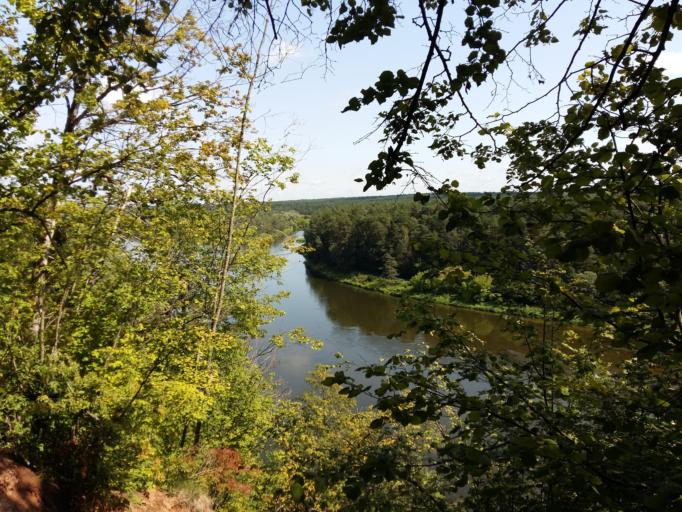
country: LT
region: Kauno apskritis
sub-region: Kauno rajonas
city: Karmelava
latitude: 55.0187
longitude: 24.1074
